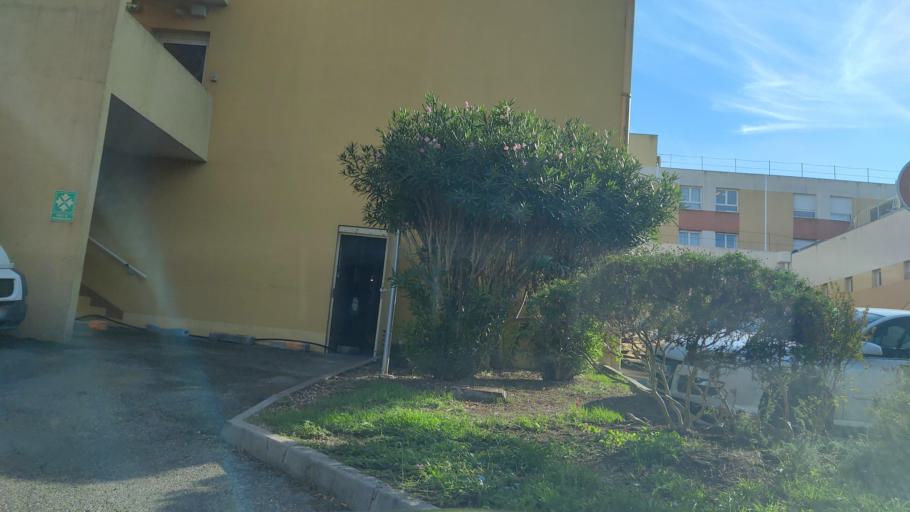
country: FR
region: Provence-Alpes-Cote d'Azur
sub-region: Departement du Var
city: La Seyne-sur-Mer
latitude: 43.0766
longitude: 5.8825
